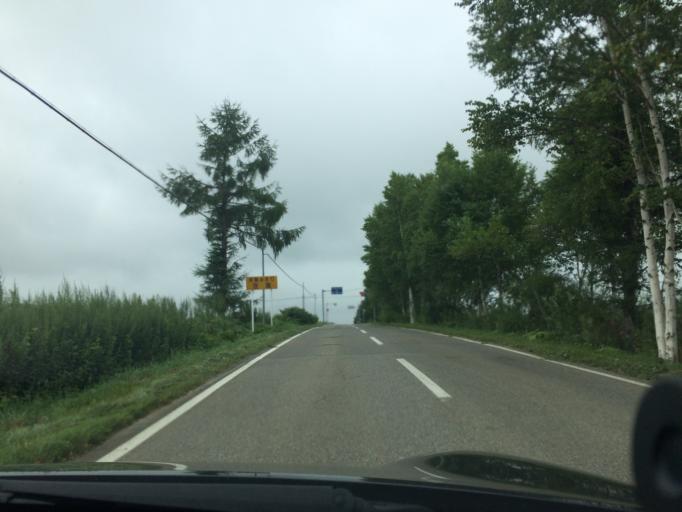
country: JP
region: Hokkaido
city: Otofuke
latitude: 42.9935
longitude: 143.0865
